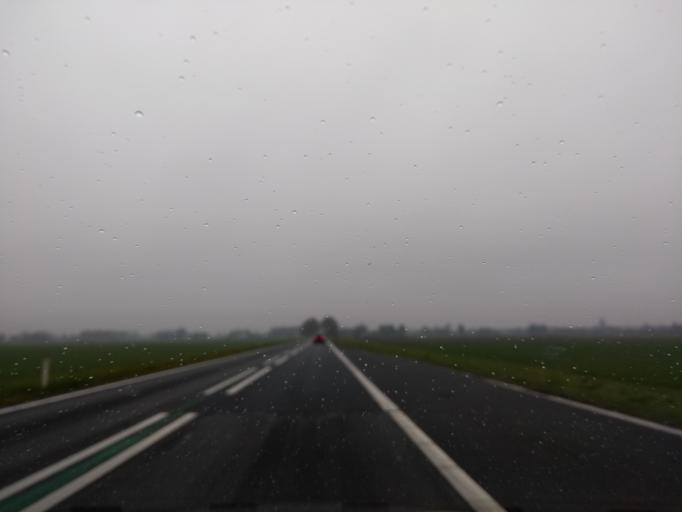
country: NL
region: Overijssel
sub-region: Gemeente Twenterand
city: Vroomshoop
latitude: 52.4931
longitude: 6.5908
